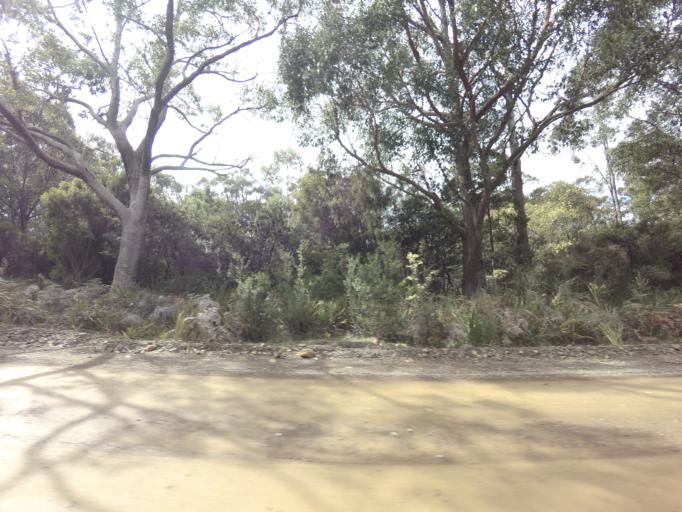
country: AU
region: Tasmania
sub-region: Huon Valley
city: Geeveston
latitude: -43.4467
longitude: 146.9051
